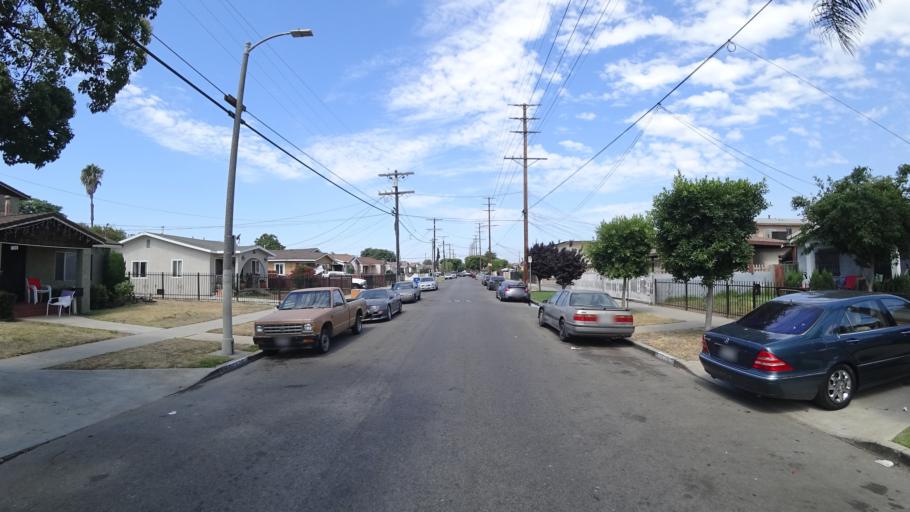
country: US
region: California
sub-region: Los Angeles County
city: Westmont
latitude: 33.9542
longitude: -118.2836
